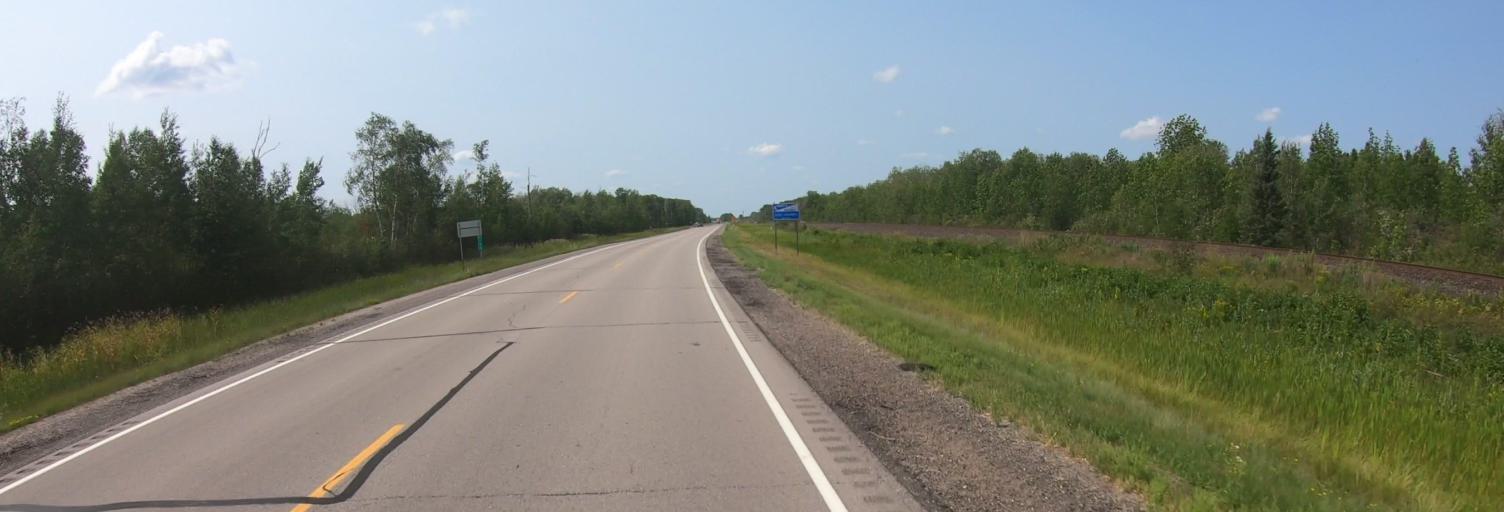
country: US
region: Minnesota
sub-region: Lake of the Woods County
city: Baudette
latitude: 48.7107
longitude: -94.7104
